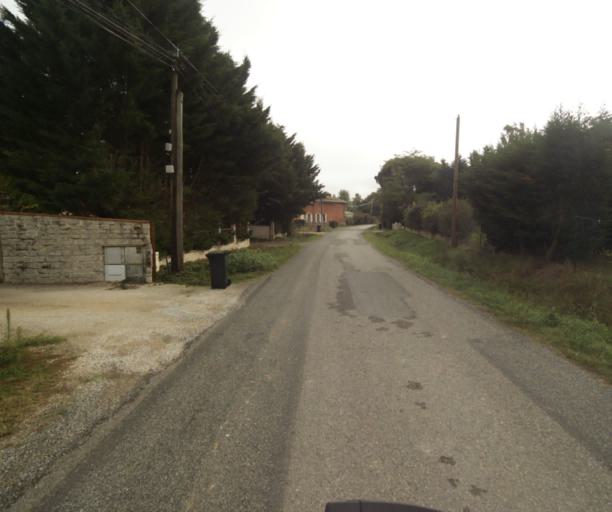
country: FR
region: Midi-Pyrenees
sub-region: Departement du Tarn-et-Garonne
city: Campsas
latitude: 43.8916
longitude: 1.3396
